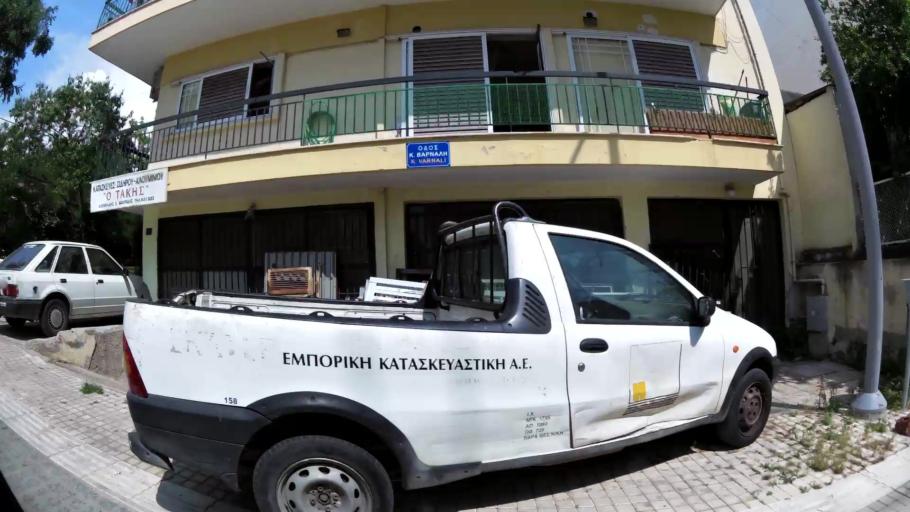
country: GR
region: Central Macedonia
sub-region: Nomos Thessalonikis
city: Stavroupoli
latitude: 40.6658
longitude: 22.9381
